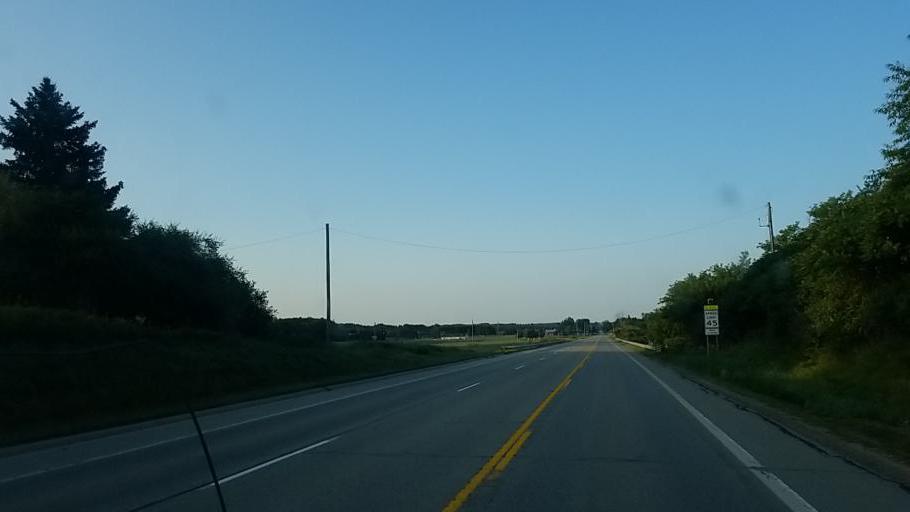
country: US
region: Michigan
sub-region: Isabella County
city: Lake Isabella
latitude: 43.6685
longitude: -85.1464
